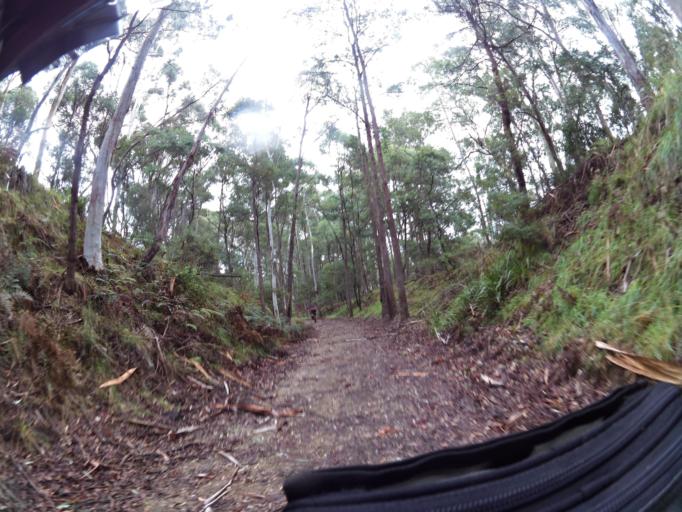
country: AU
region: New South Wales
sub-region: Greater Hume Shire
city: Holbrook
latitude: -36.1469
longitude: 147.4610
